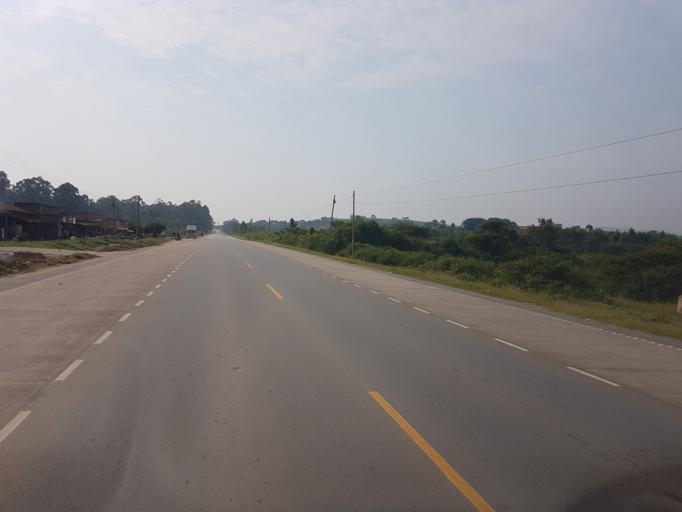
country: UG
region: Western Region
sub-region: Mbarara District
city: Bwizibwera
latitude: -0.6392
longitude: 30.5500
